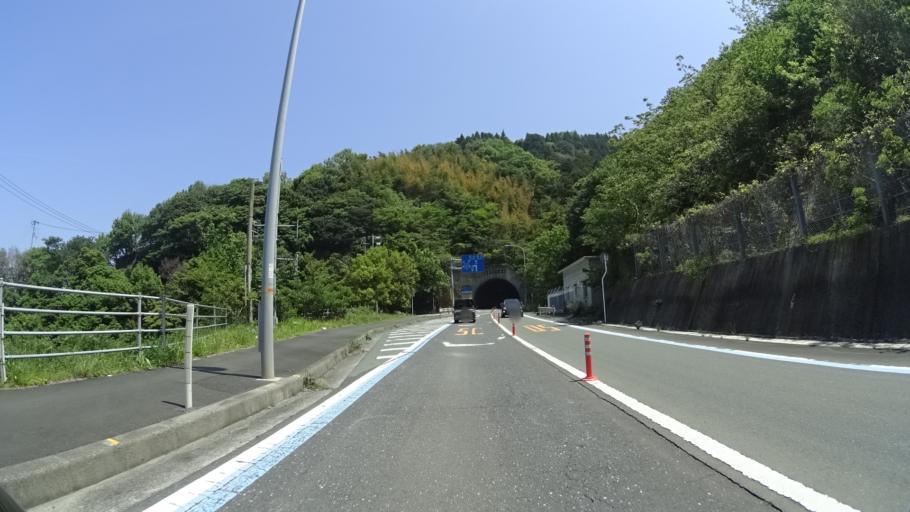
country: JP
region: Ehime
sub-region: Nishiuwa-gun
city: Ikata-cho
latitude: 33.5275
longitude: 132.3919
